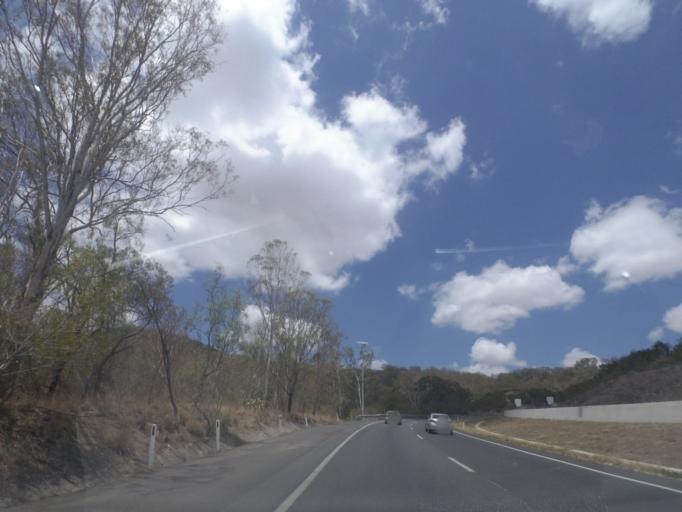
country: AU
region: Queensland
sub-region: Toowoomba
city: East Toowoomba
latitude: -27.5704
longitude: 151.9884
